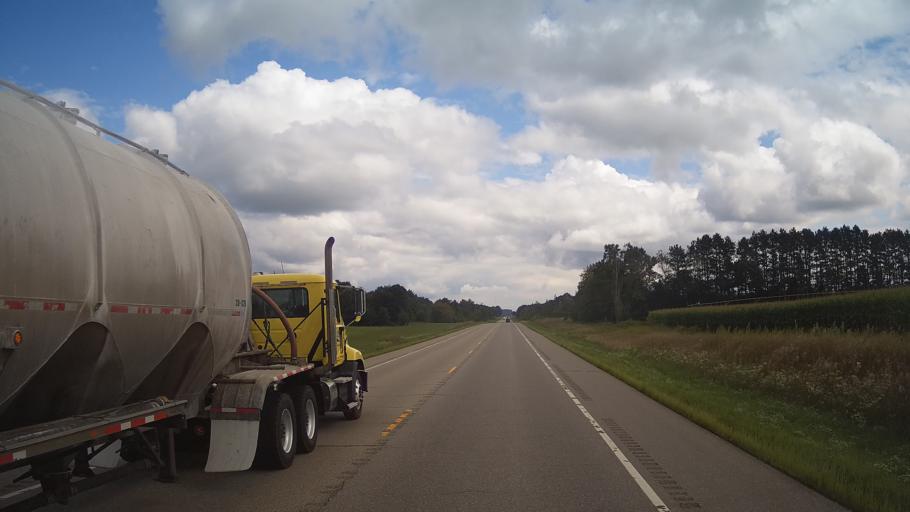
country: US
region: Wisconsin
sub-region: Adams County
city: Friendship
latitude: 44.0220
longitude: -89.6354
